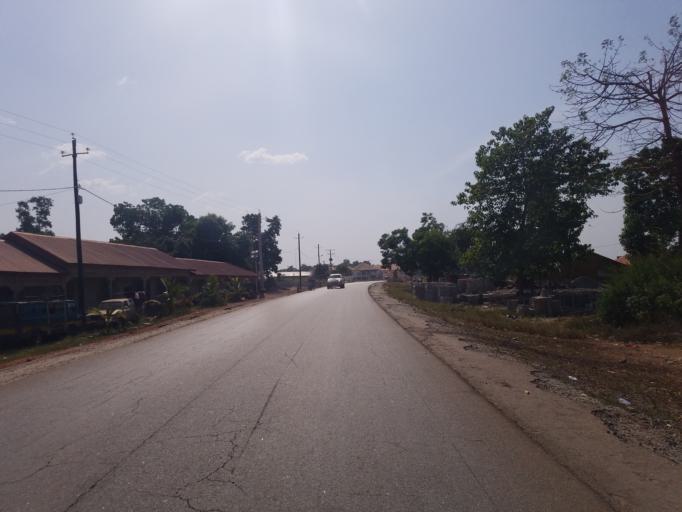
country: GN
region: Boke
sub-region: Fria
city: Fria
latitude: 10.0749
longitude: -13.7034
